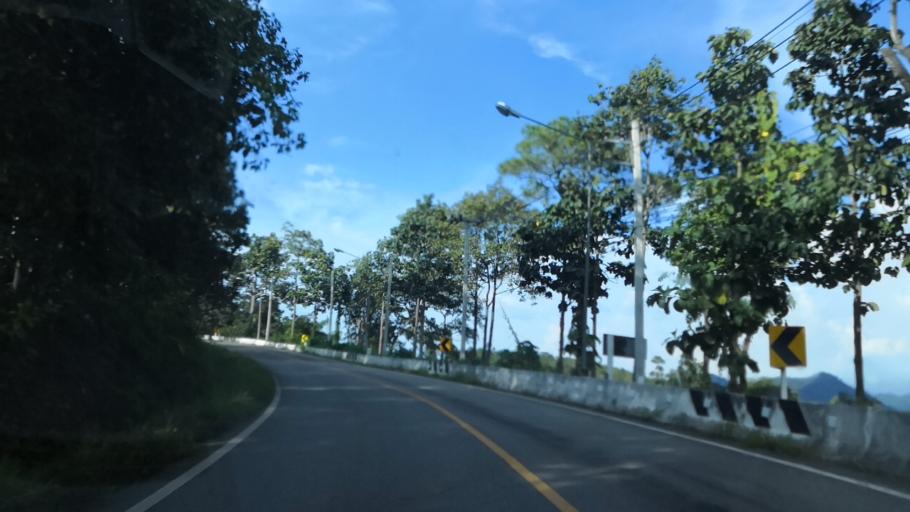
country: TH
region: Mae Hong Son
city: Khun Yuam
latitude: 18.7451
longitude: 97.9274
